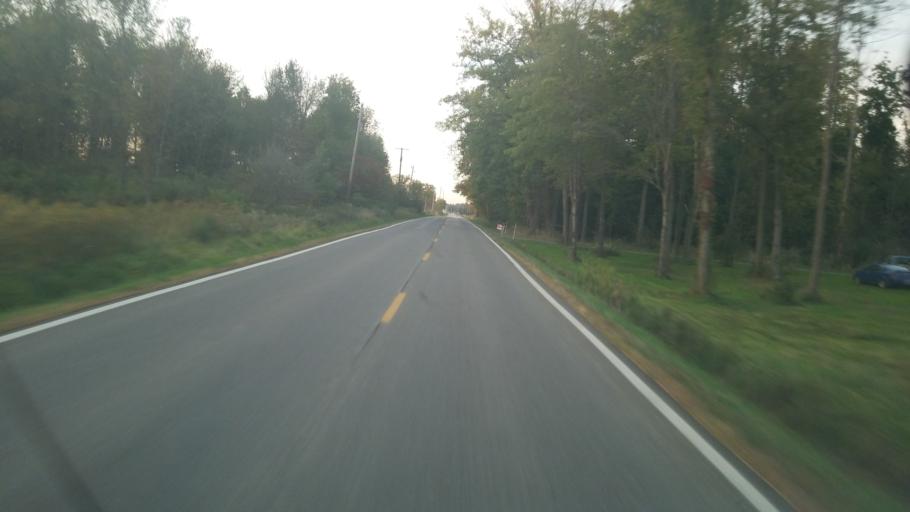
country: US
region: Ohio
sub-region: Ashtabula County
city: Andover
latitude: 41.6545
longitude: -80.6670
